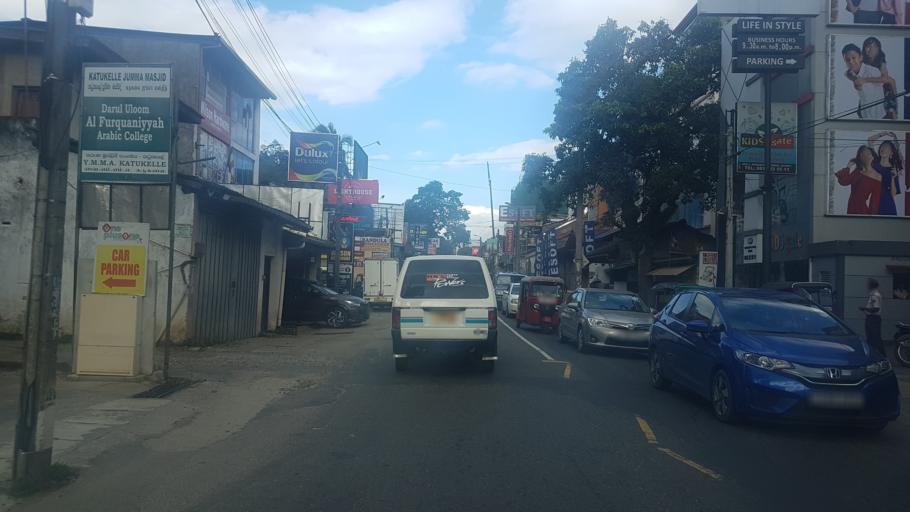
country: LK
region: Central
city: Kandy
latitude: 7.2841
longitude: 80.6240
